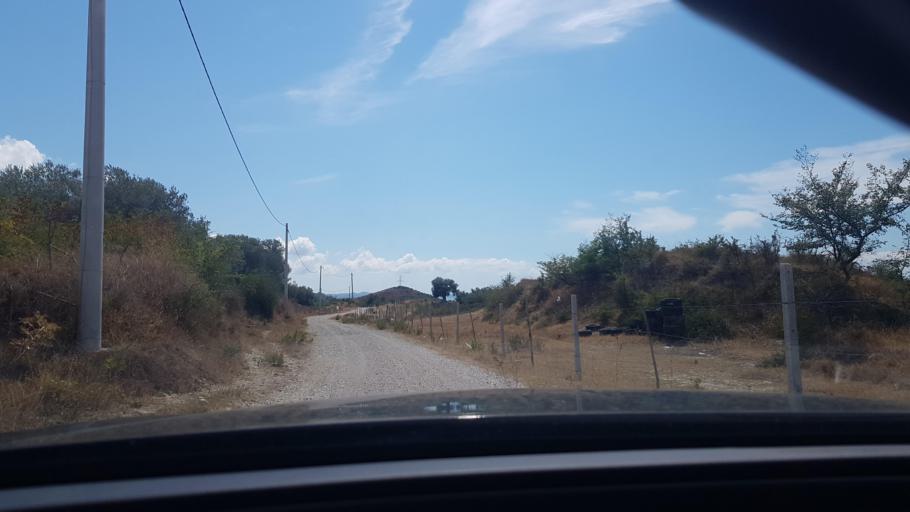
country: AL
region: Tirane
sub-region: Rrethi i Kavajes
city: Golem
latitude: 41.2855
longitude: 19.5475
